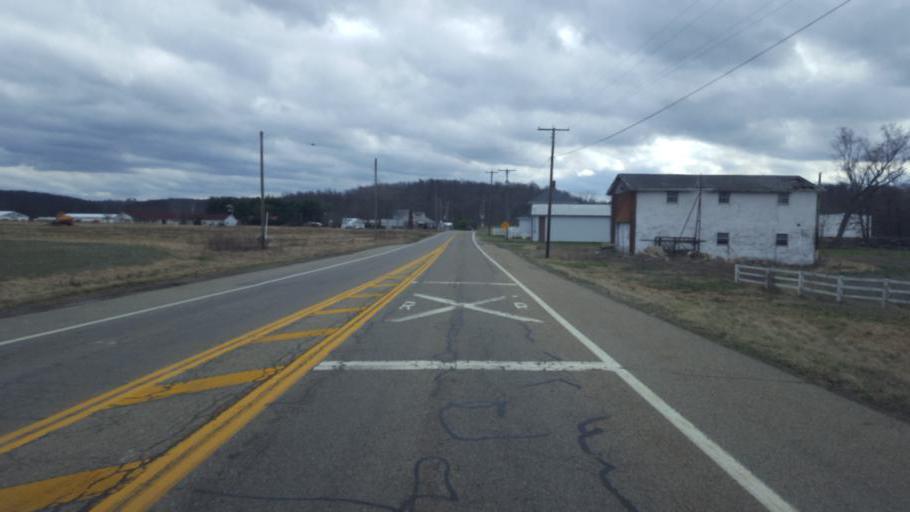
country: US
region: Ohio
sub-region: Muskingum County
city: Frazeysburg
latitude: 40.1015
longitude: -82.1729
